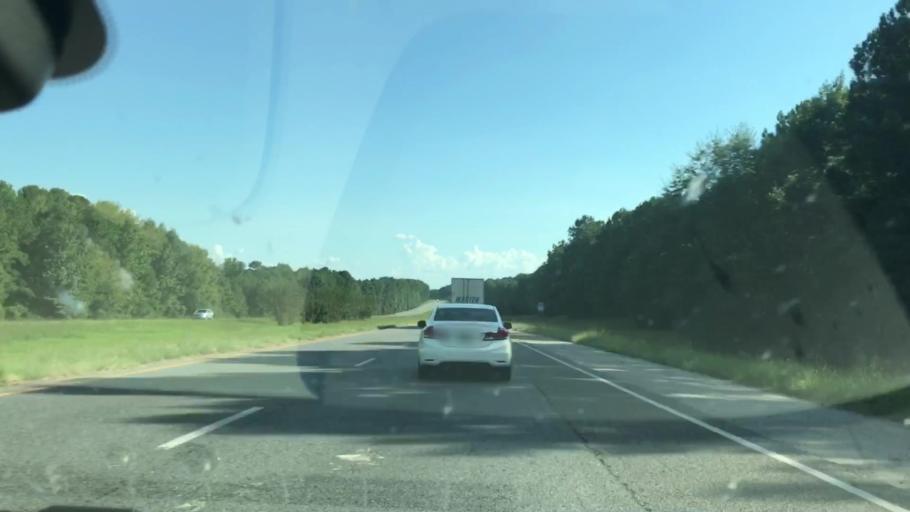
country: US
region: Georgia
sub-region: Troup County
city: La Grange
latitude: 32.9550
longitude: -84.9566
